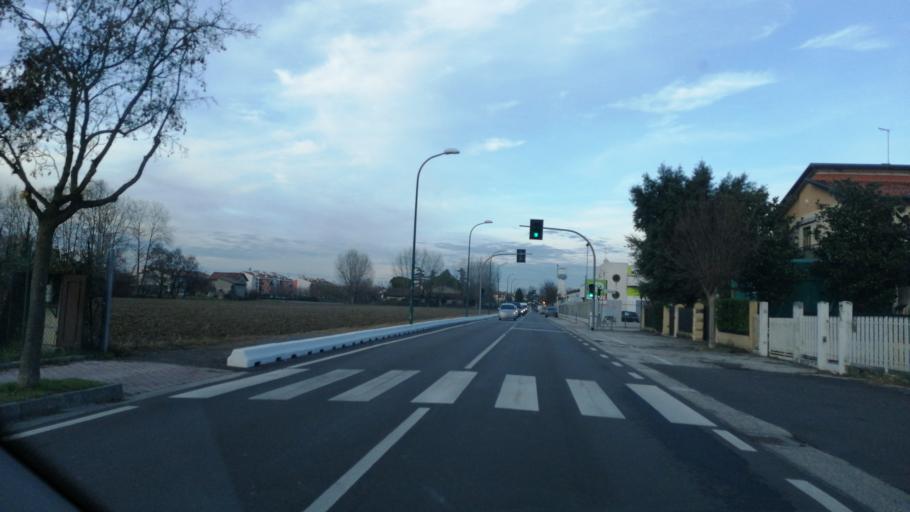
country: IT
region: Veneto
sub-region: Provincia di Venezia
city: Zelarino
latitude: 45.4905
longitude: 12.2106
